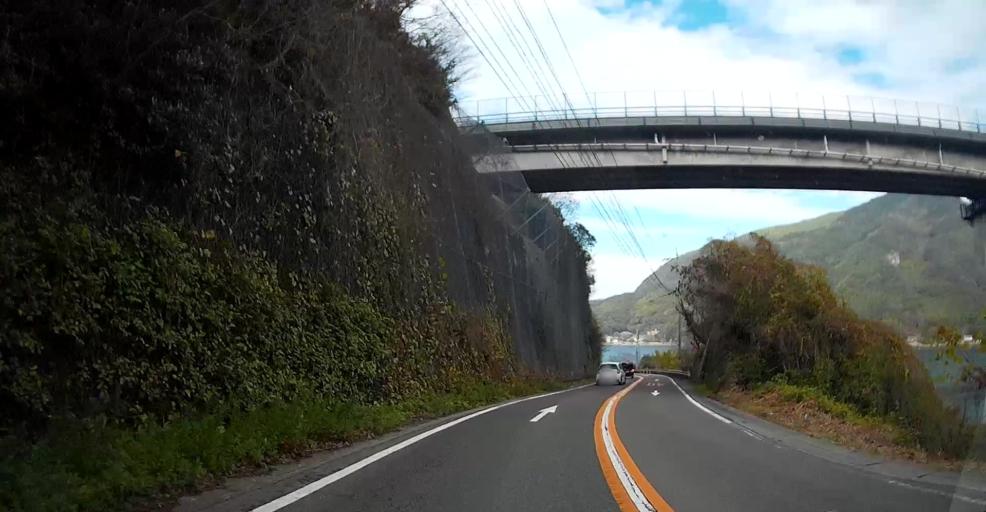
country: JP
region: Kumamoto
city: Yatsushiro
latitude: 32.6141
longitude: 130.4543
